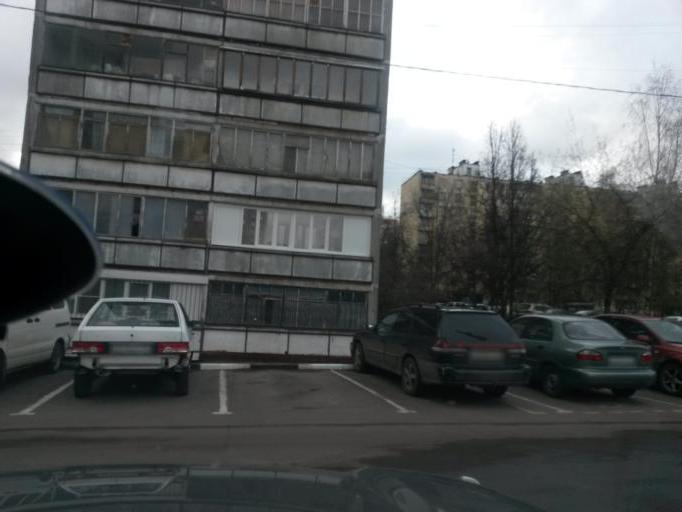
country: RU
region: Moscow
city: Annino
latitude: 55.5641
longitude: 37.5775
